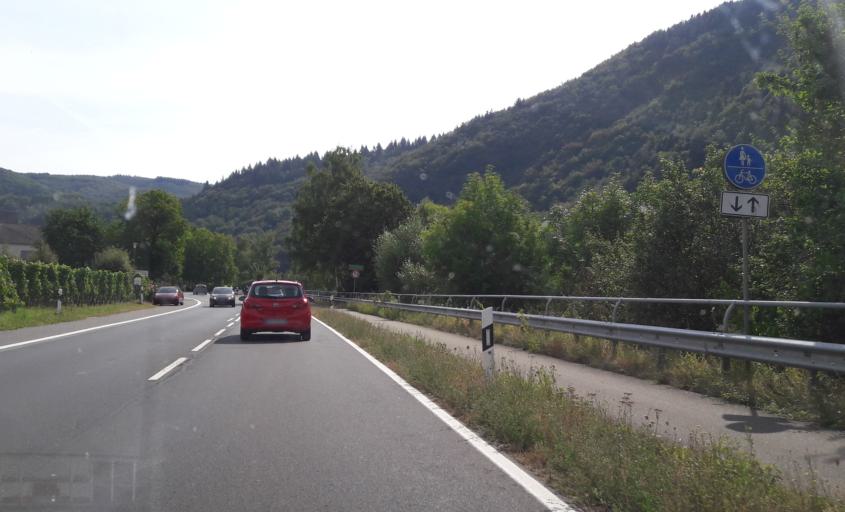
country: DE
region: Rheinland-Pfalz
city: Ellenz-Poltersdorf
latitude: 50.1072
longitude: 7.2208
